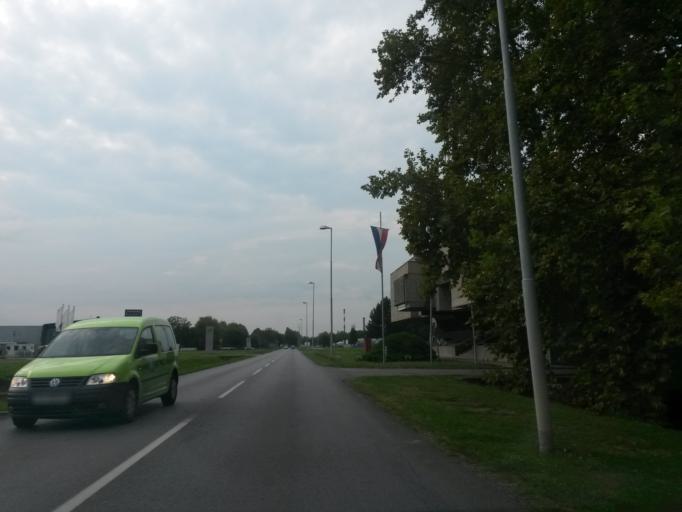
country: HR
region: Osjecko-Baranjska
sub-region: Grad Osijek
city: Osijek
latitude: 45.5434
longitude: 18.7387
